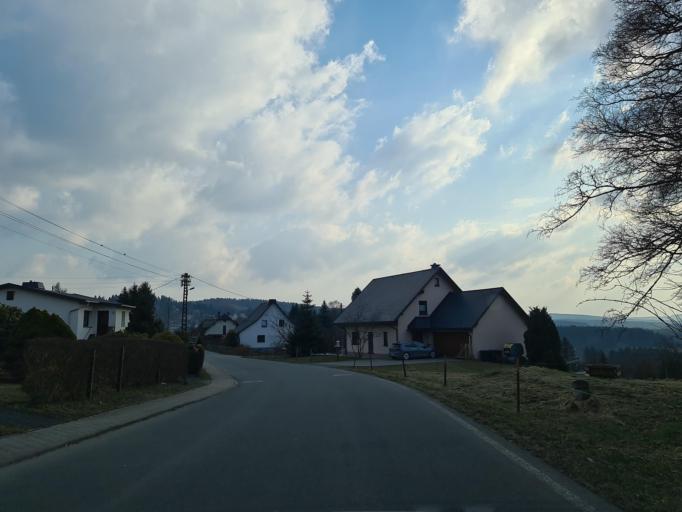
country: DE
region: Saxony
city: Rodewisch
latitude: 50.5083
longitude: 12.4525
